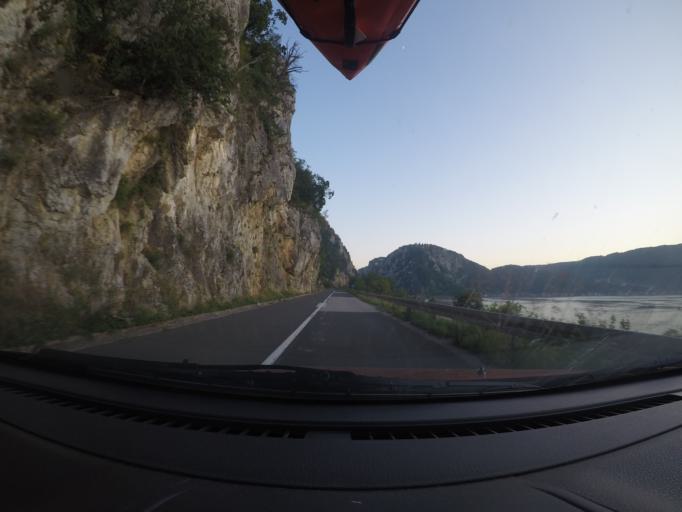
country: RO
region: Mehedinti
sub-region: Comuna Dubova
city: Dubova
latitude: 44.6251
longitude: 22.2791
